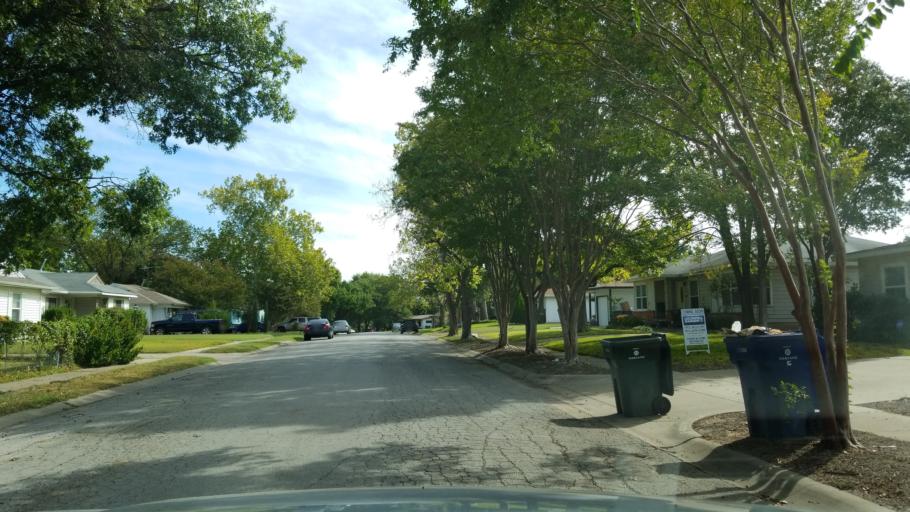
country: US
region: Texas
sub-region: Dallas County
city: Garland
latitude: 32.8985
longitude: -96.6567
